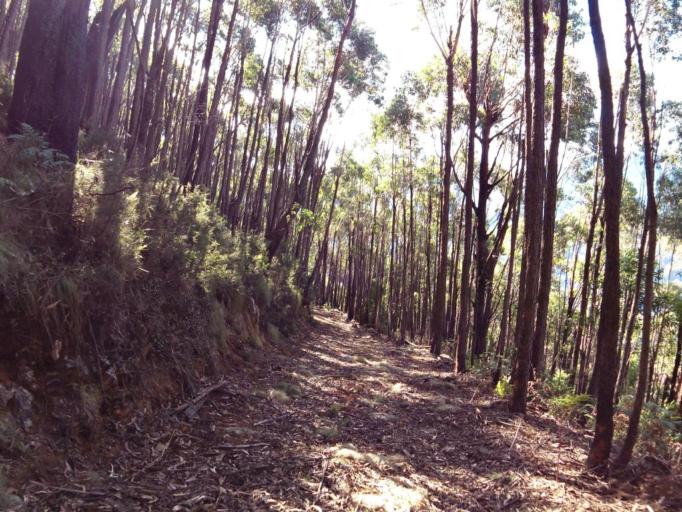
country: AU
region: Victoria
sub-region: Yarra Ranges
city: Millgrove
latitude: -37.7609
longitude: 145.6745
